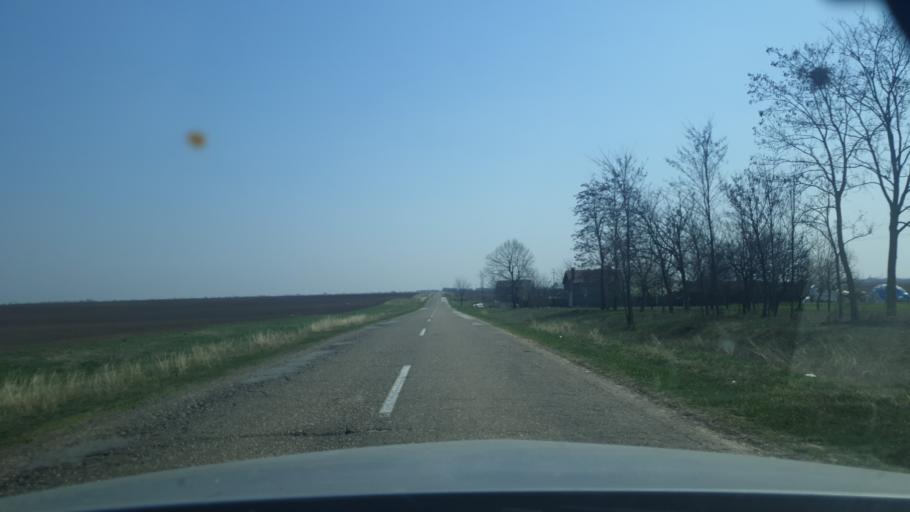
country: RS
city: Sasinci
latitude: 45.0327
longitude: 19.7472
